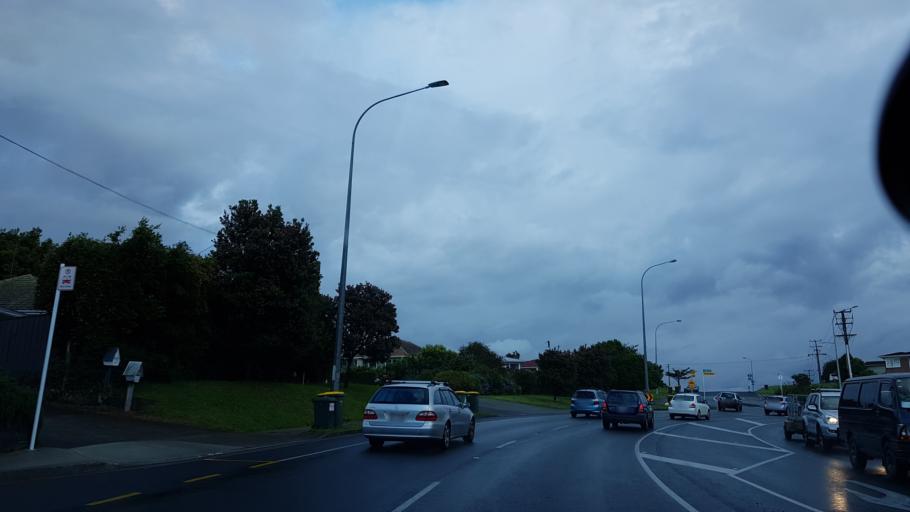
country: NZ
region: Auckland
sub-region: Auckland
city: North Shore
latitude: -36.7737
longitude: 174.7208
